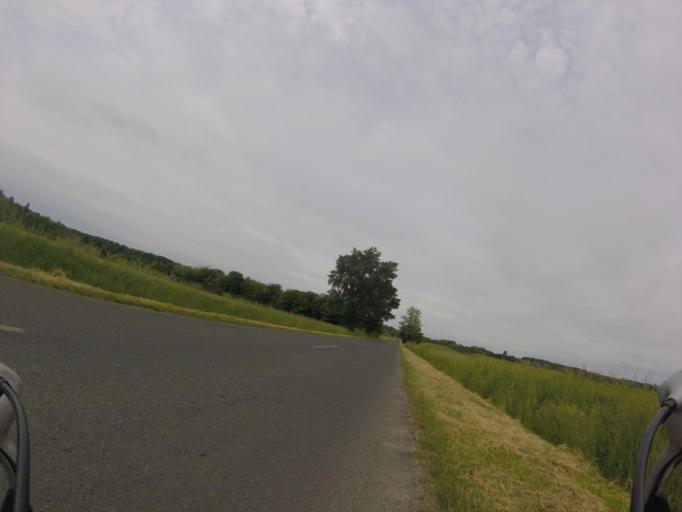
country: HU
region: Zala
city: Turje
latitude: 46.9400
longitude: 17.1546
